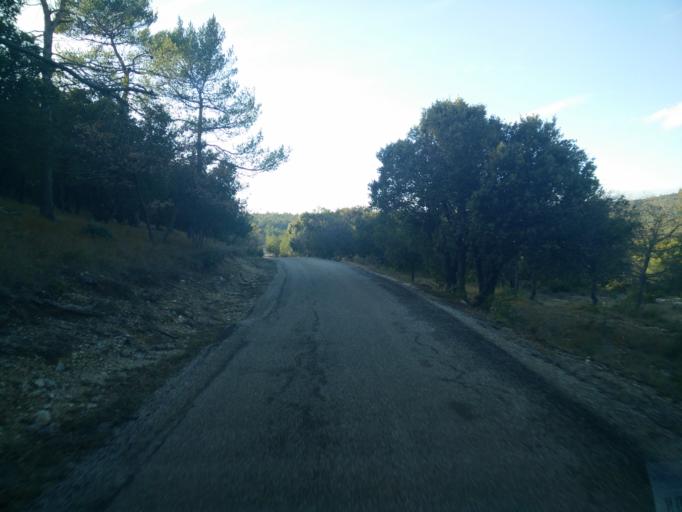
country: FR
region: Provence-Alpes-Cote d'Azur
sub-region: Departement du Var
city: Le Revest-les-Eaux
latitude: 43.2269
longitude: 5.9260
